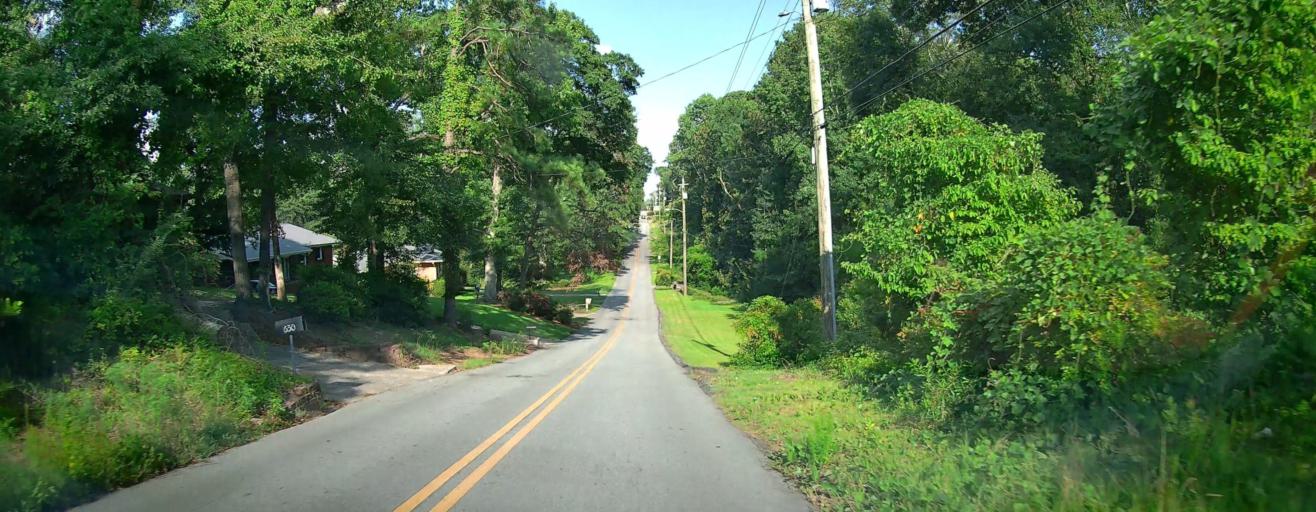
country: US
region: Georgia
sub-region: Houston County
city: Centerville
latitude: 32.5994
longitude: -83.6506
